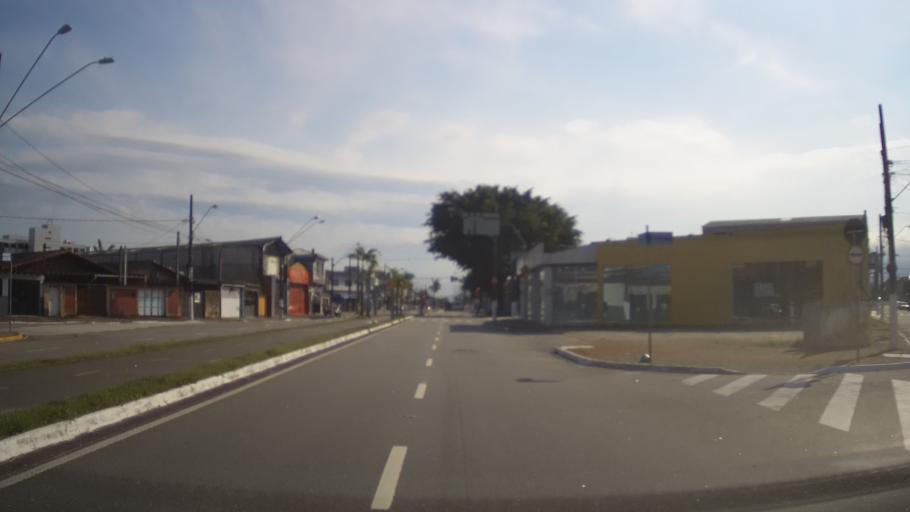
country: BR
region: Sao Paulo
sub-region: Praia Grande
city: Praia Grande
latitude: -24.0025
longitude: -46.4165
